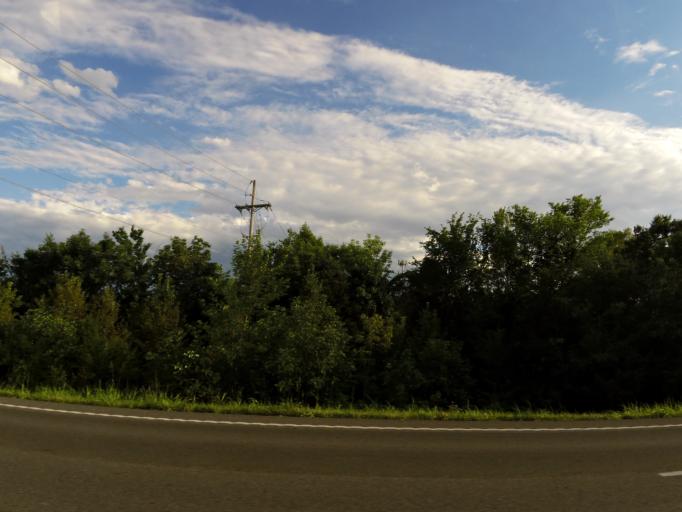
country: US
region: Missouri
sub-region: Saint Charles County
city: Weldon Spring
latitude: 38.7098
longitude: -90.6808
